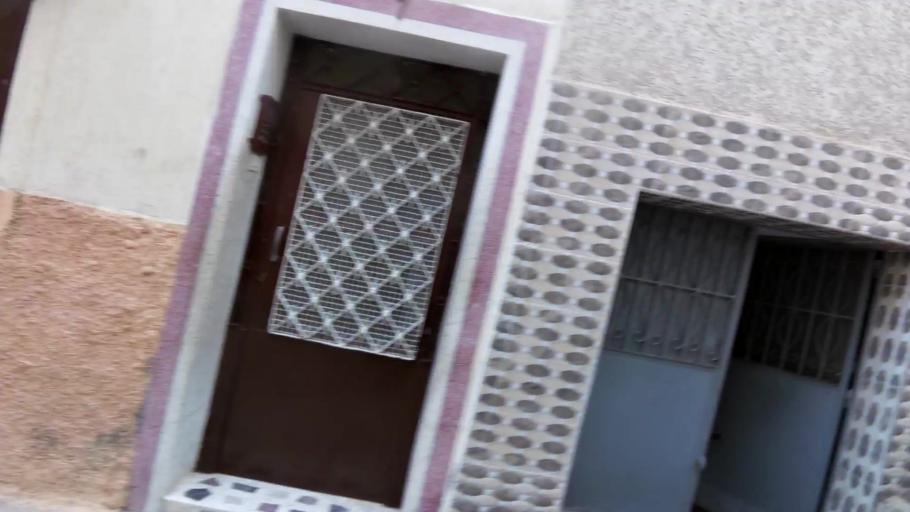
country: MA
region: Tanger-Tetouan
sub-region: Tanger-Assilah
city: Tangier
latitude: 35.7620
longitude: -5.8254
